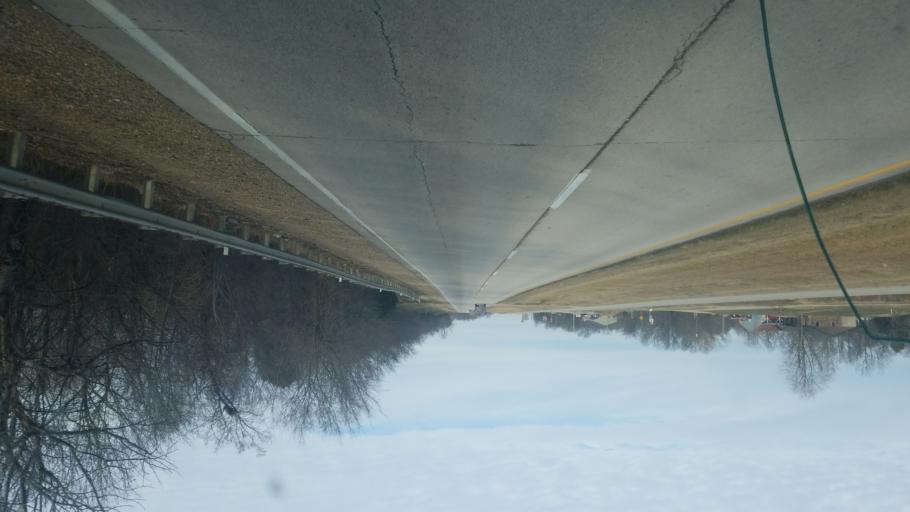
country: US
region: Missouri
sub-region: Stoddard County
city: Dexter
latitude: 36.8273
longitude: -89.9413
